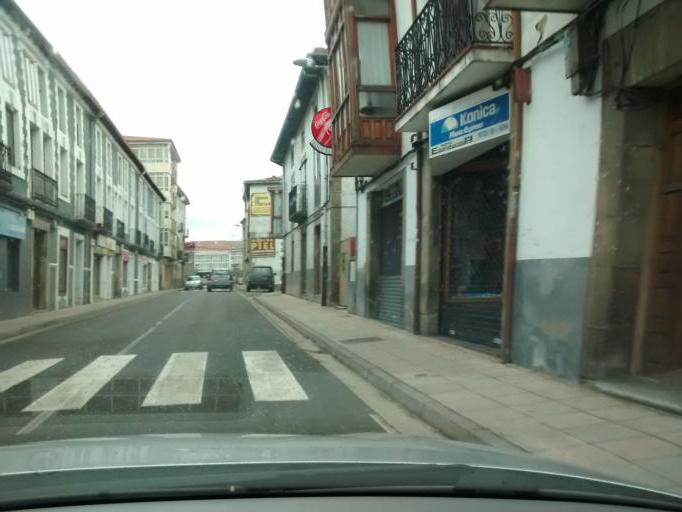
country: ES
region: Castille and Leon
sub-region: Provincia de Burgos
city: Espinosa de los Monteros
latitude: 43.0780
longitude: -3.5524
